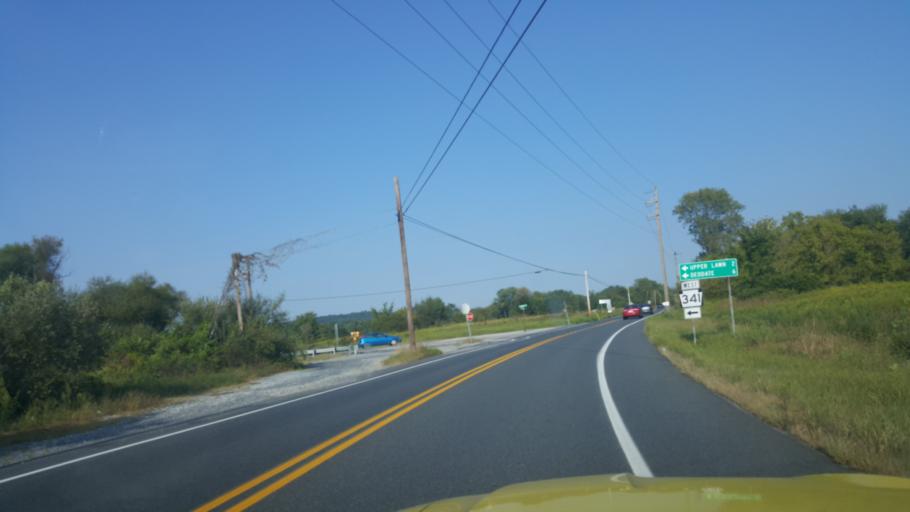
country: US
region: Pennsylvania
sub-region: Lebanon County
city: Campbelltown
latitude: 40.2373
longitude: -76.5254
